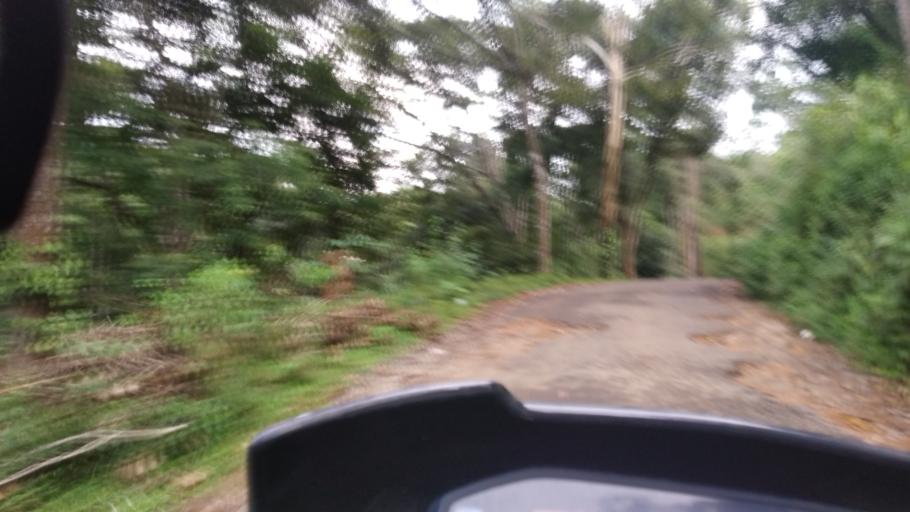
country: IN
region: Tamil Nadu
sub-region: Theni
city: Gudalur
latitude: 9.5500
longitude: 77.0565
